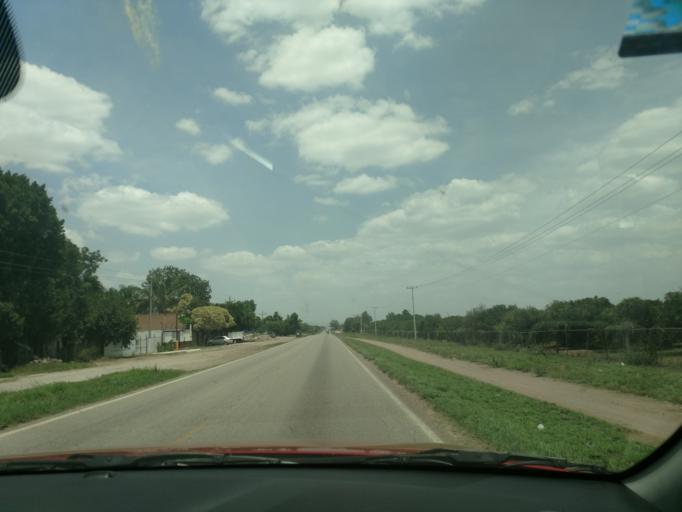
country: MX
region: San Luis Potosi
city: Ciudad Fernandez
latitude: 21.9495
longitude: -100.0610
